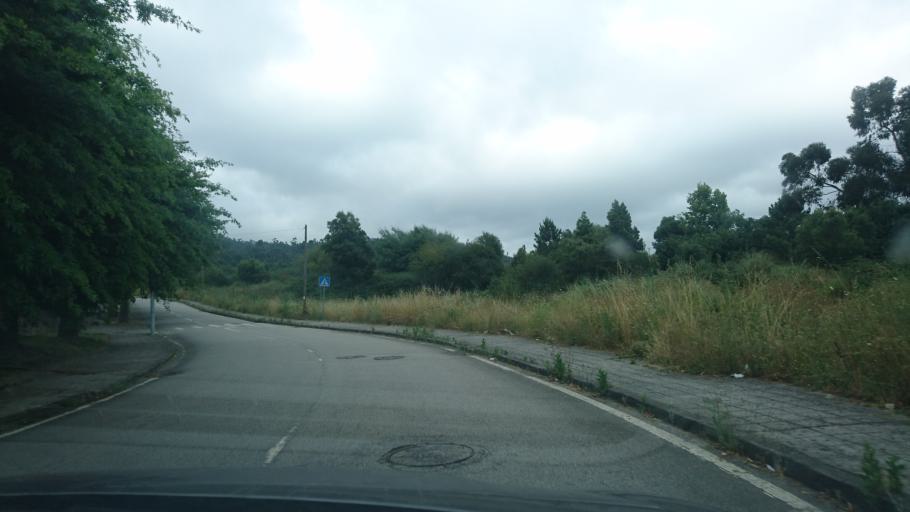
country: PT
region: Porto
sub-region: Valongo
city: Valongo
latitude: 41.1947
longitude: -8.4907
